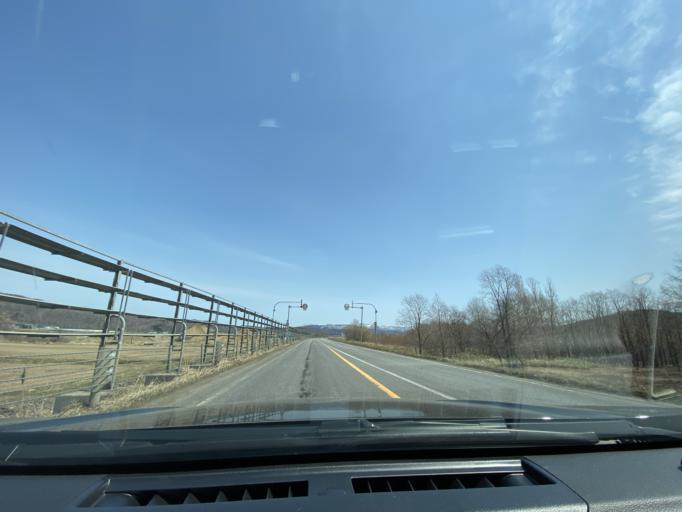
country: JP
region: Hokkaido
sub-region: Asahikawa-shi
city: Asahikawa
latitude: 43.8975
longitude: 142.5274
